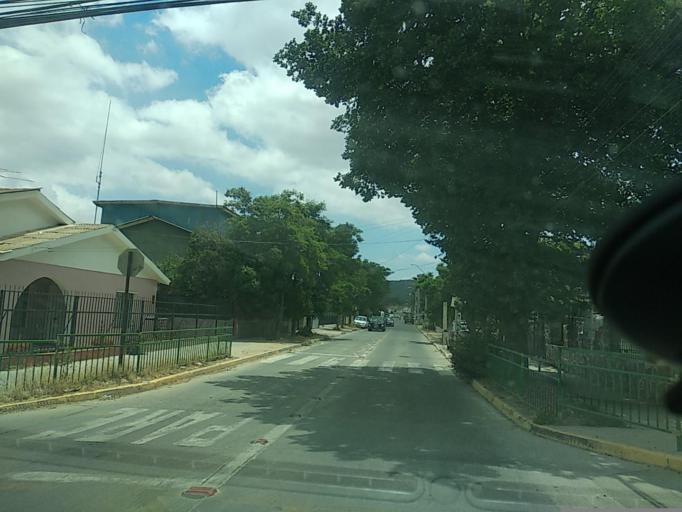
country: CL
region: Valparaiso
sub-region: Provincia de Marga Marga
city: Villa Alemana
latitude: -33.0362
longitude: -71.4056
